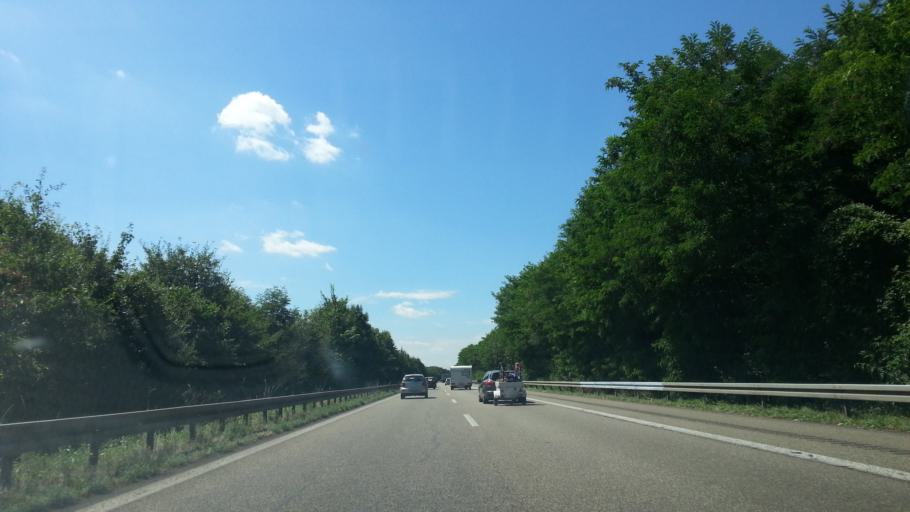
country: DE
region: Baden-Wuerttemberg
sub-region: Freiburg Region
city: Umkirch
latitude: 48.0069
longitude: 7.7625
